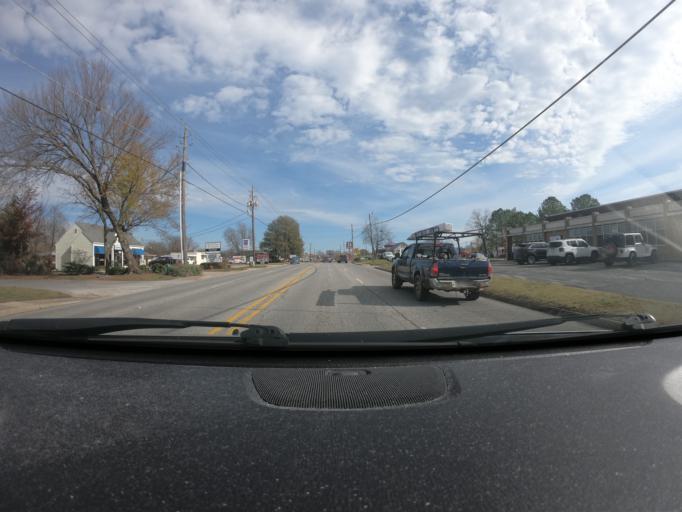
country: US
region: Arkansas
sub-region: Benton County
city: Rogers
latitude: 36.3337
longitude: -94.1318
